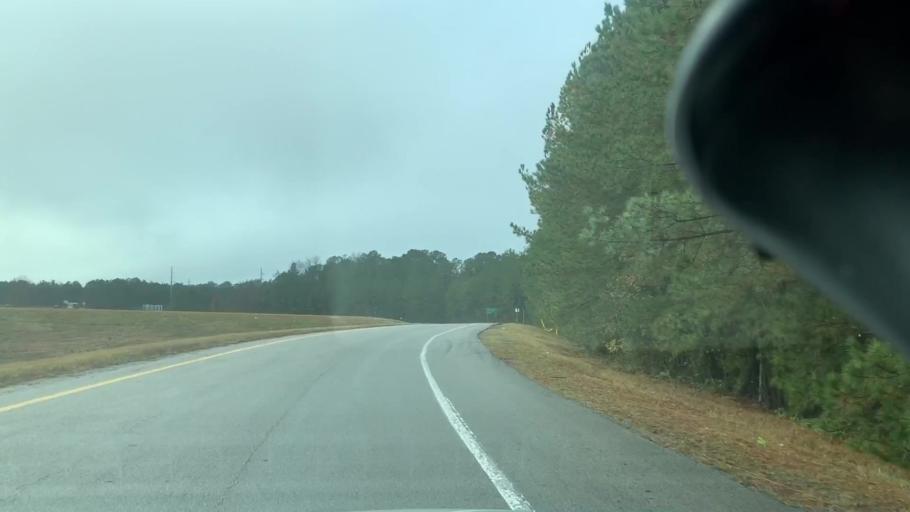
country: US
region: South Carolina
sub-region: Richland County
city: Woodfield
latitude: 34.0541
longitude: -80.9234
